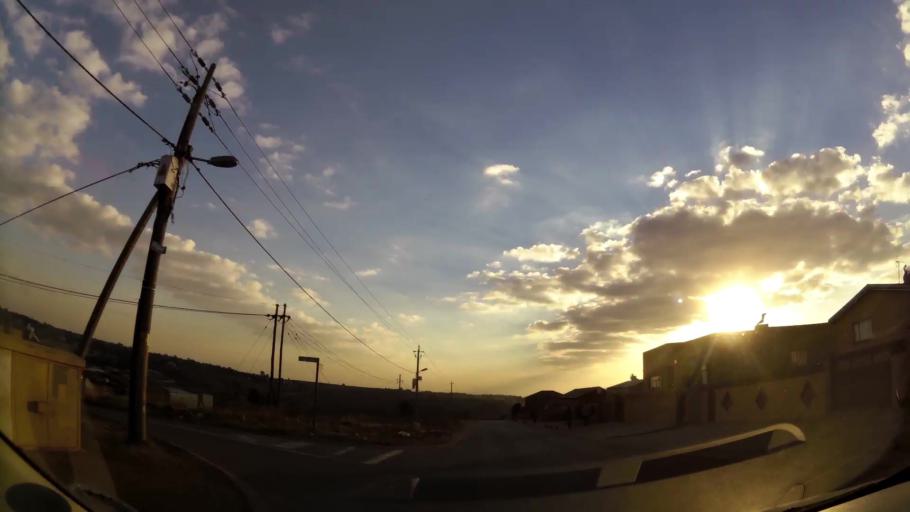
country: ZA
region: Gauteng
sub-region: West Rand District Municipality
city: Krugersdorp
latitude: -26.0811
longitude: 27.7515
